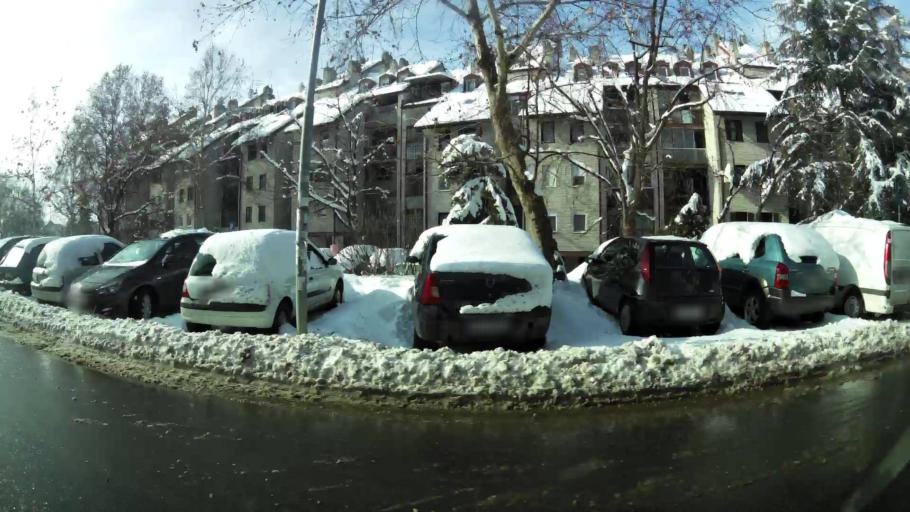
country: RS
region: Central Serbia
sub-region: Belgrade
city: Zvezdara
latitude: 44.7870
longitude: 20.5466
